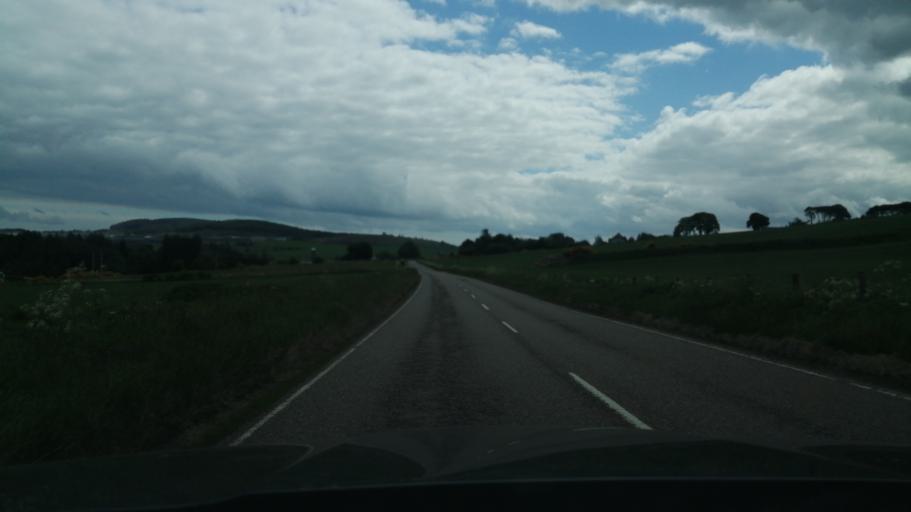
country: GB
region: Scotland
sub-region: Moray
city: Fochabers
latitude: 57.5469
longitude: -3.1014
